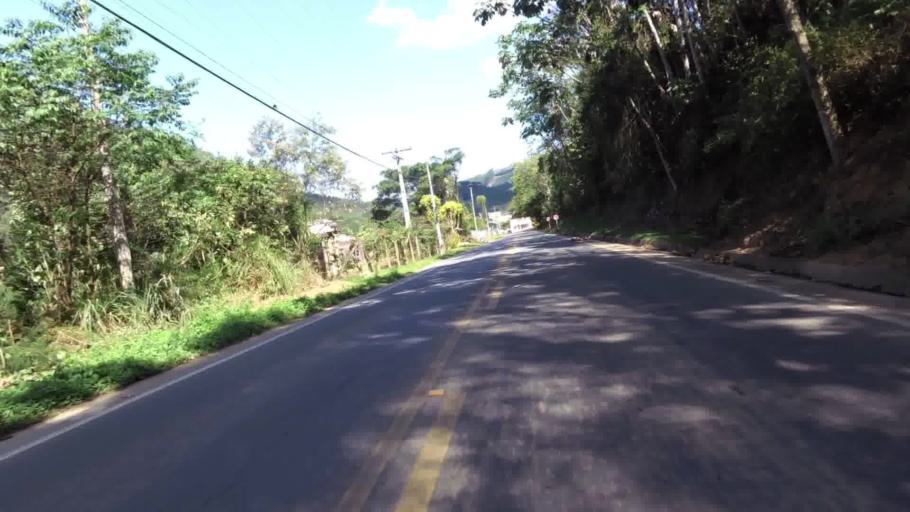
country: BR
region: Espirito Santo
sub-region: Marechal Floriano
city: Marechal Floriano
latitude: -20.4505
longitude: -40.7856
